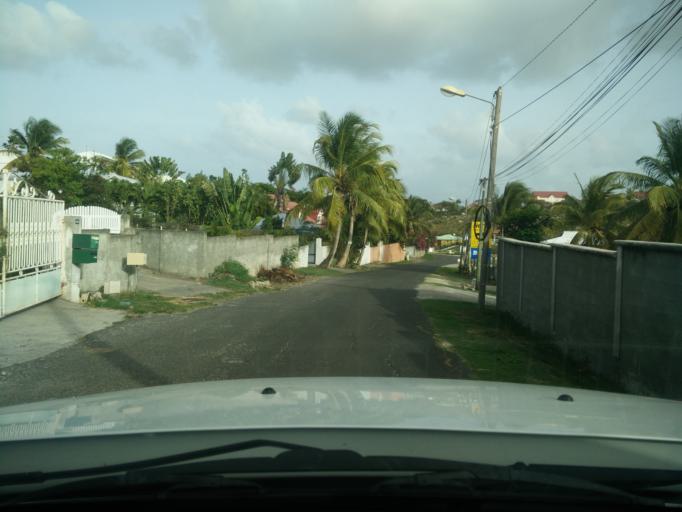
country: GP
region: Guadeloupe
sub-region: Guadeloupe
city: Sainte-Anne
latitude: 16.2452
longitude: -61.3311
